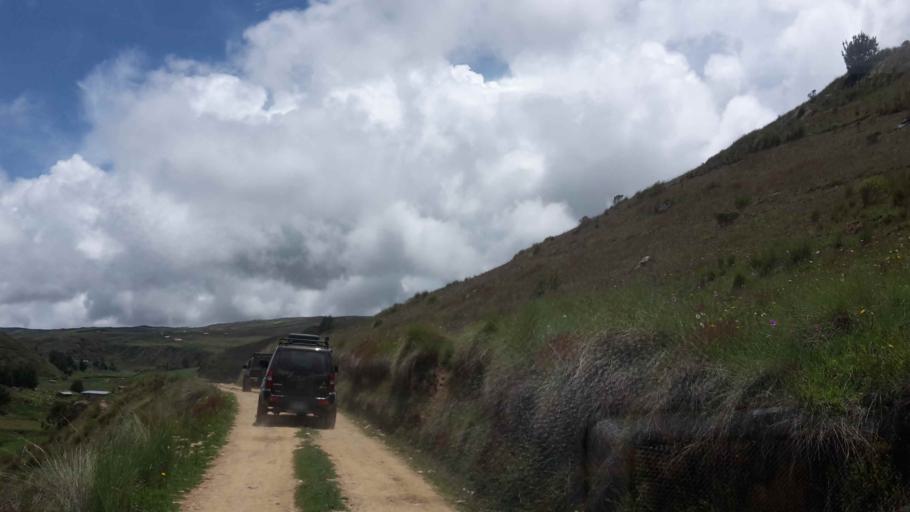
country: BO
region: Cochabamba
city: Cochabamba
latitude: -17.1882
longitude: -66.0733
